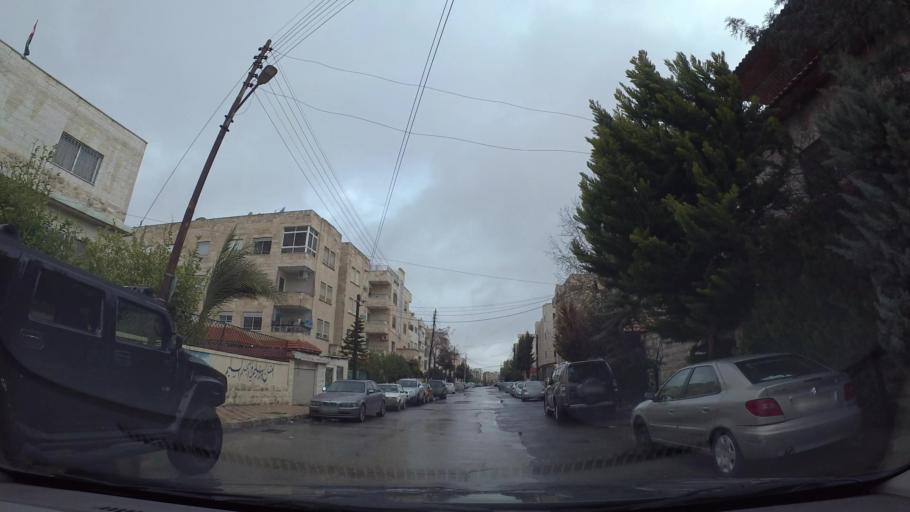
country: JO
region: Amman
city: Wadi as Sir
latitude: 31.9644
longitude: 35.8619
